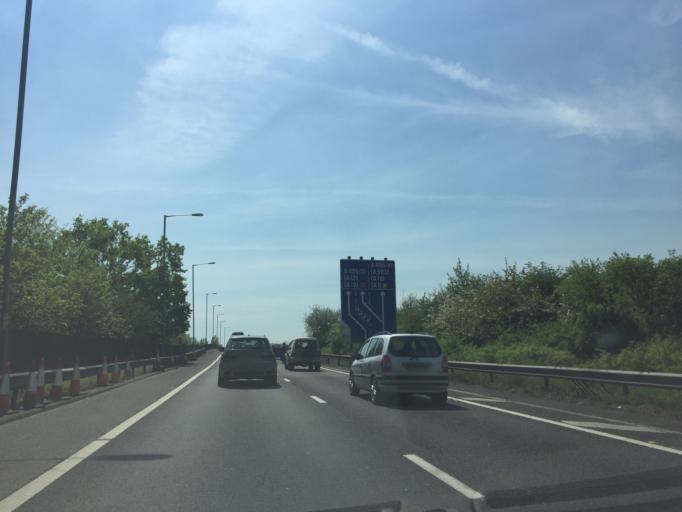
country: GB
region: England
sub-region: Greater London
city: Woodford Green
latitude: 51.6016
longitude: 0.0483
